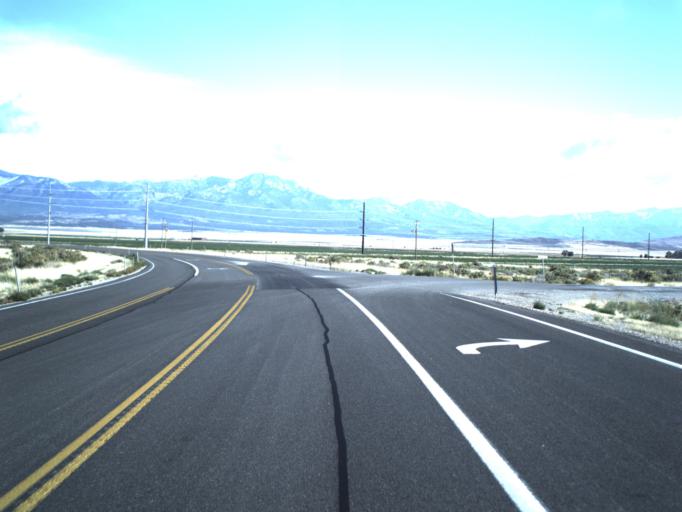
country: US
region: Utah
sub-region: Millard County
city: Fillmore
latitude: 39.1197
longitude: -112.3559
